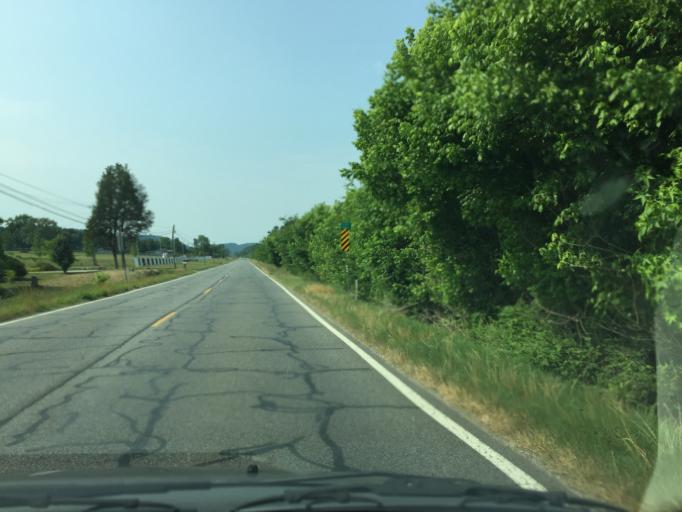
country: US
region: Georgia
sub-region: Catoosa County
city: Ringgold
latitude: 34.9543
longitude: -85.1040
